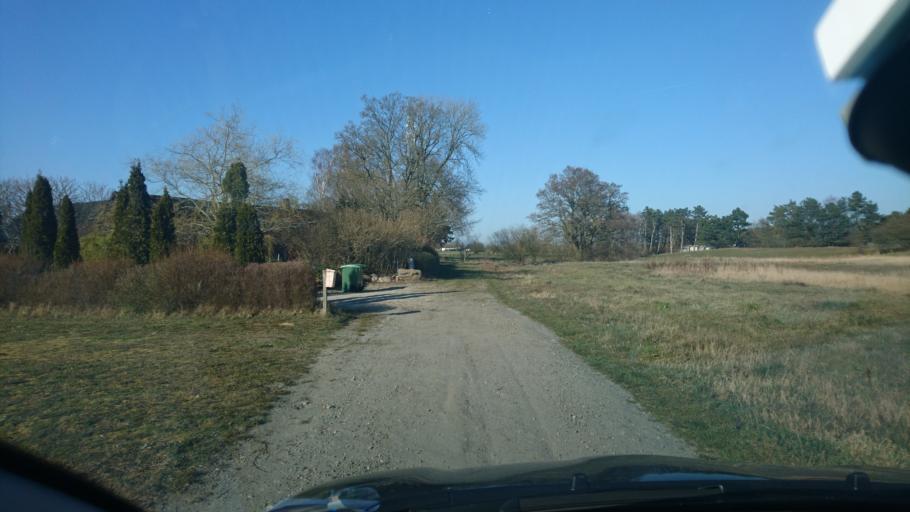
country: SE
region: Skane
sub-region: Simrishamns Kommun
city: Simrishamn
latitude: 55.4203
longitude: 14.2073
